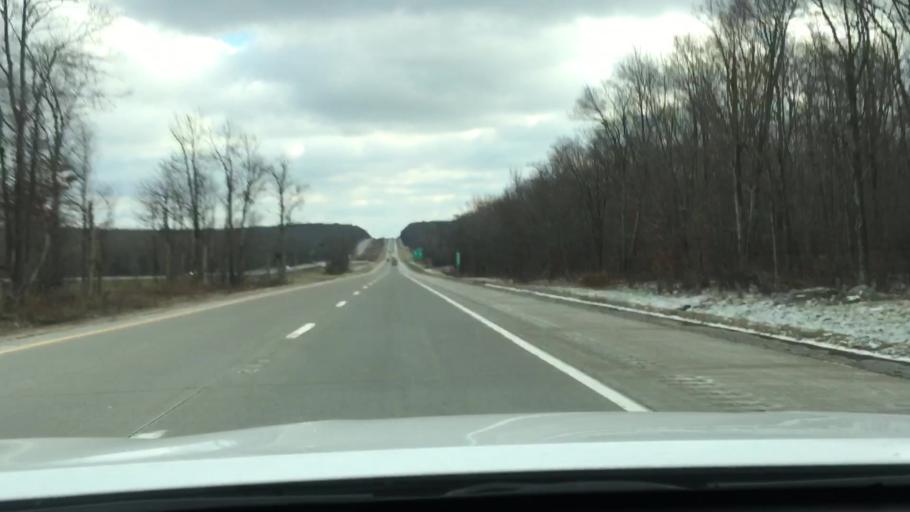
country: US
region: Pennsylvania
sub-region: Monroe County
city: Pocono Pines
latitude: 41.2083
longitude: -75.4662
